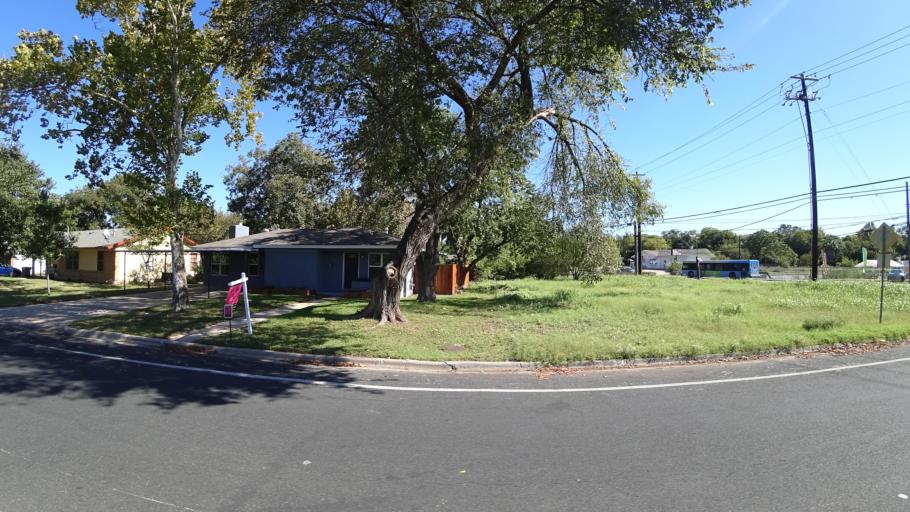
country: US
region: Texas
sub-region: Travis County
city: Austin
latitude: 30.3005
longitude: -97.6863
